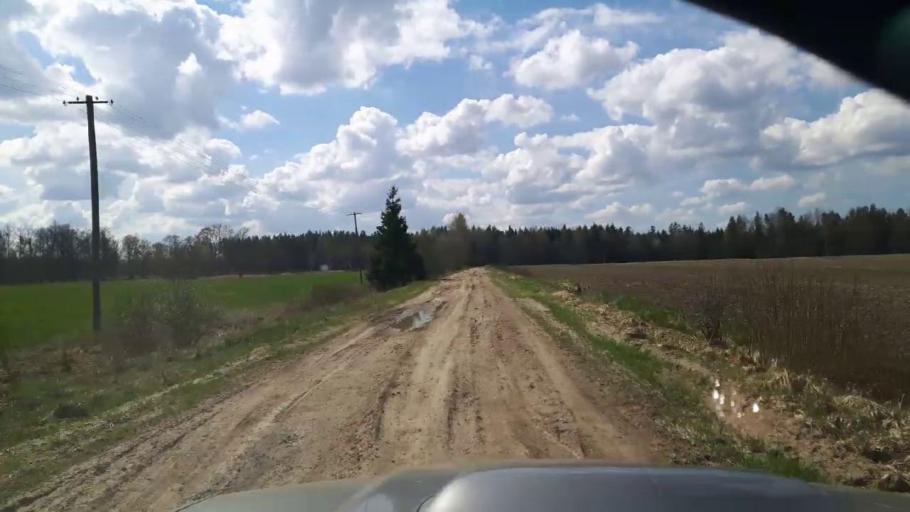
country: EE
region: Paernumaa
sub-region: Vaendra vald (alev)
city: Vandra
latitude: 58.5390
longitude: 25.0679
